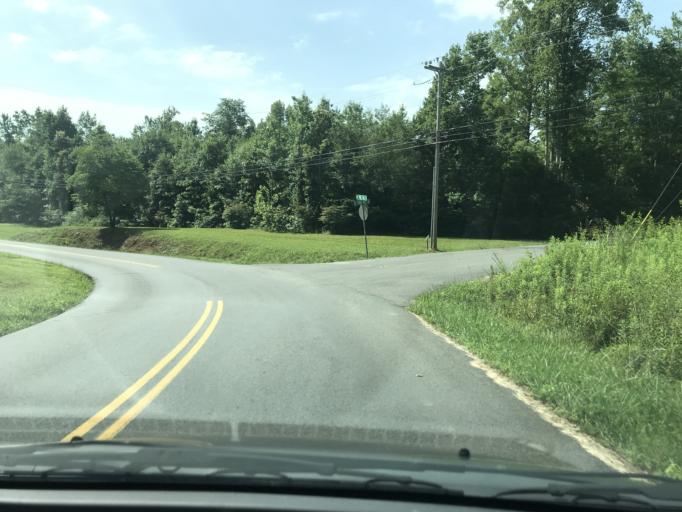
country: US
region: Tennessee
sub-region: Hamilton County
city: Apison
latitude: 35.0743
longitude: -84.9926
